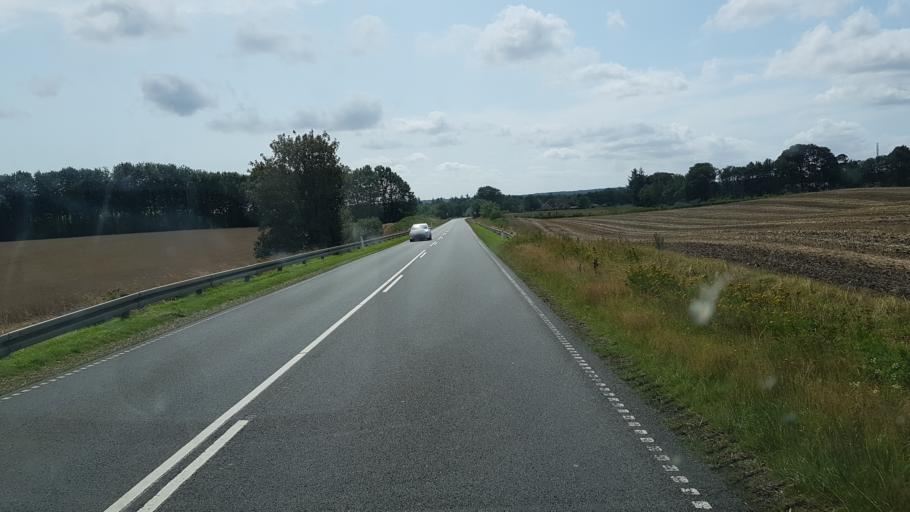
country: DK
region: South Denmark
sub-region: Vejen Kommune
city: Vejen
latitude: 55.5783
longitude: 9.1565
